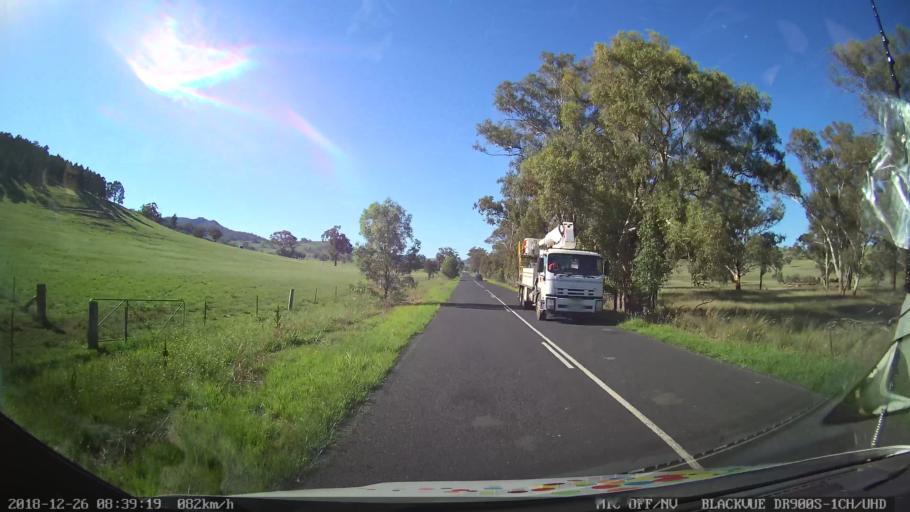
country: AU
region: New South Wales
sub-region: Mid-Western Regional
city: Kandos
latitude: -32.4520
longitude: 150.0757
